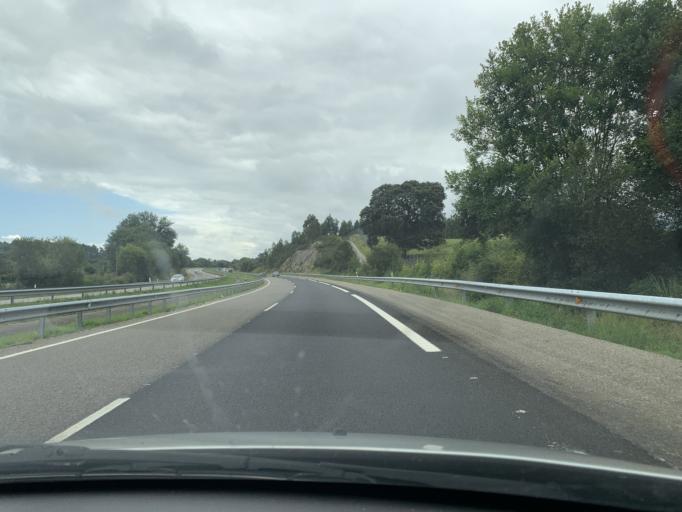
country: ES
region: Asturias
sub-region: Province of Asturias
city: Llanes
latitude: 43.4231
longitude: -4.8055
